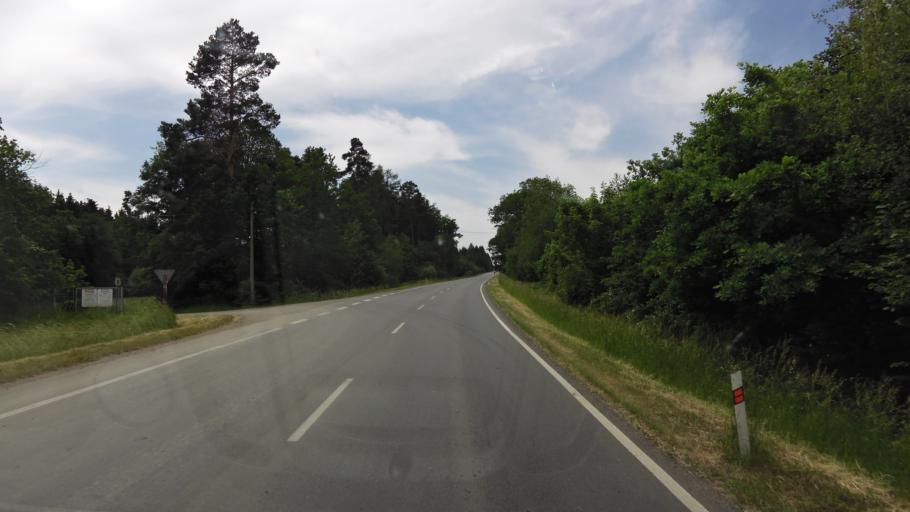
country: CZ
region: Plzensky
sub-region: Okres Rokycany
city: Rokycany
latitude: 49.7204
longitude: 13.5752
